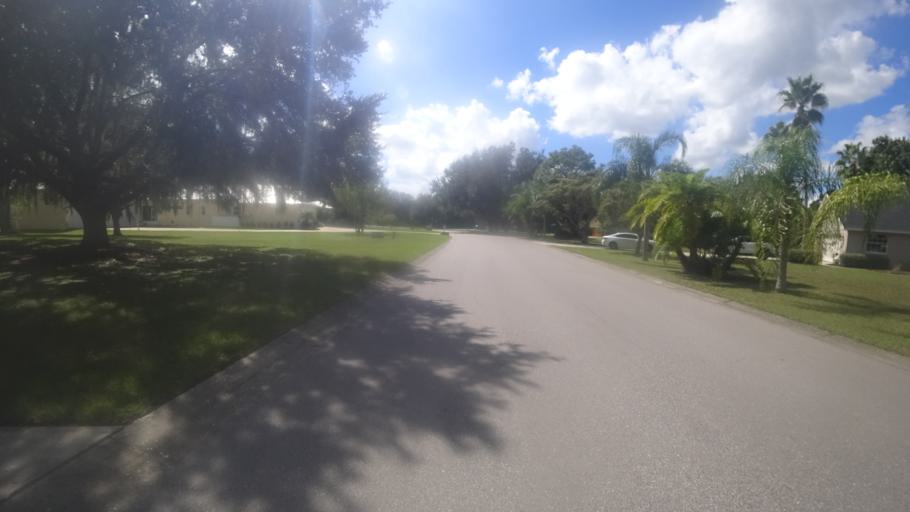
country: US
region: Florida
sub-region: Manatee County
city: Ellenton
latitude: 27.4939
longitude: -82.4055
